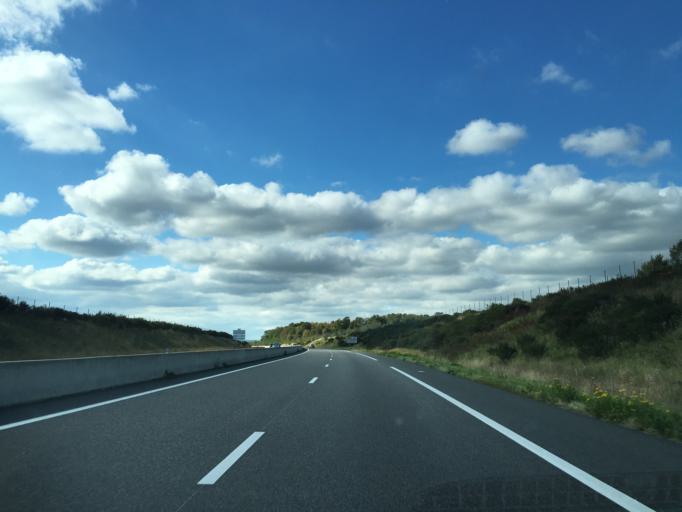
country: FR
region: Lorraine
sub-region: Departement de Meurthe-et-Moselle
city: Gerbeviller
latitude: 48.5266
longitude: 6.6332
